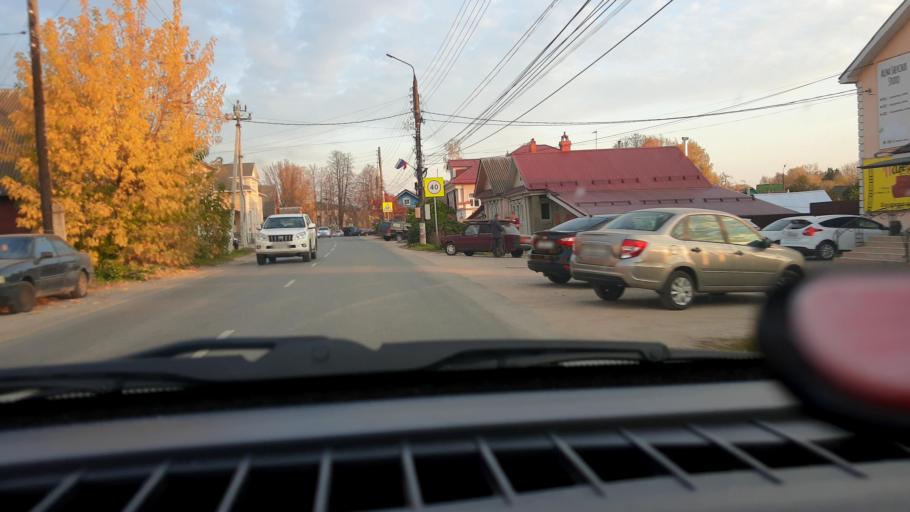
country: RU
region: Nizjnij Novgorod
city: Gorodets
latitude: 56.6436
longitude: 43.4739
